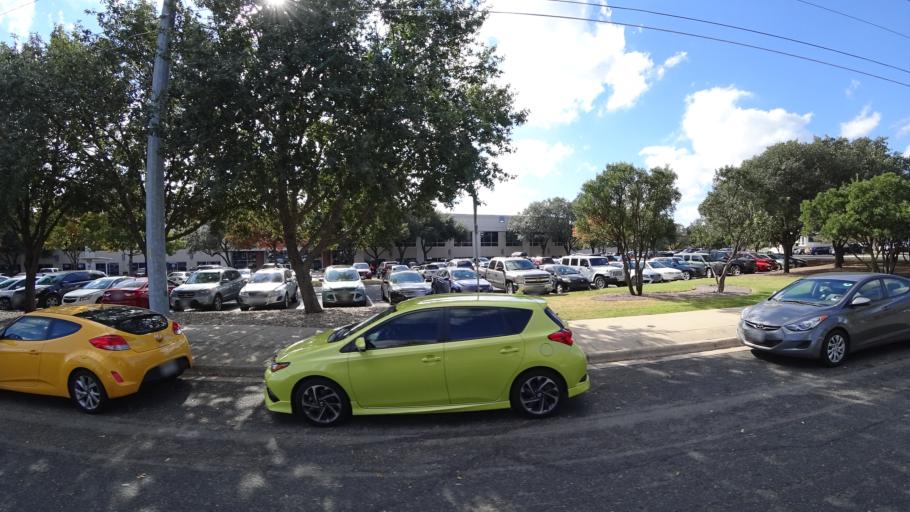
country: US
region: Texas
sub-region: Williamson County
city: Jollyville
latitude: 30.4332
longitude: -97.7363
